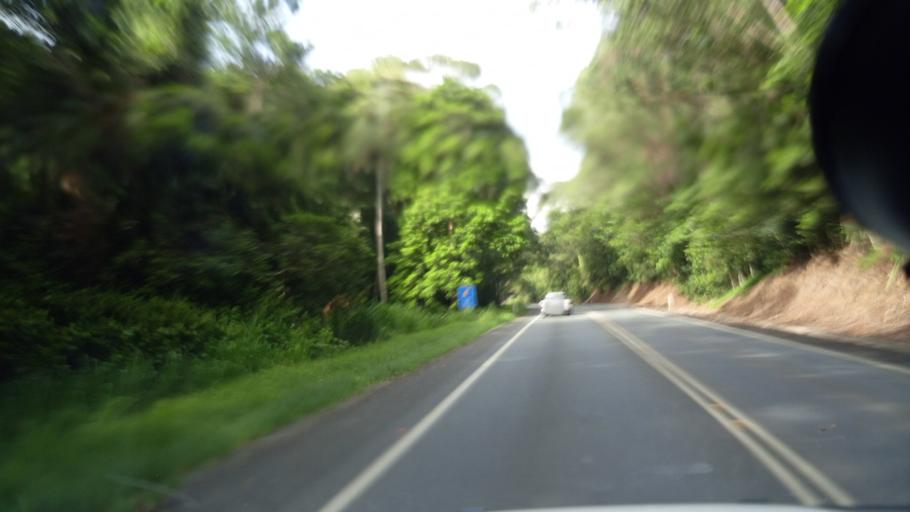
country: AU
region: Queensland
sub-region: Tablelands
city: Kuranda
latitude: -16.8206
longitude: 145.6290
